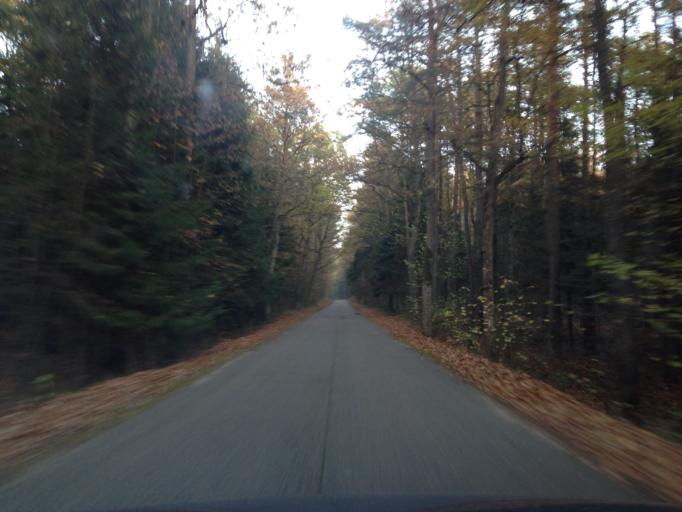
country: PL
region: Warmian-Masurian Voivodeship
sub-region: Powiat dzialdowski
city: Lidzbark
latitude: 53.2457
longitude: 19.7485
